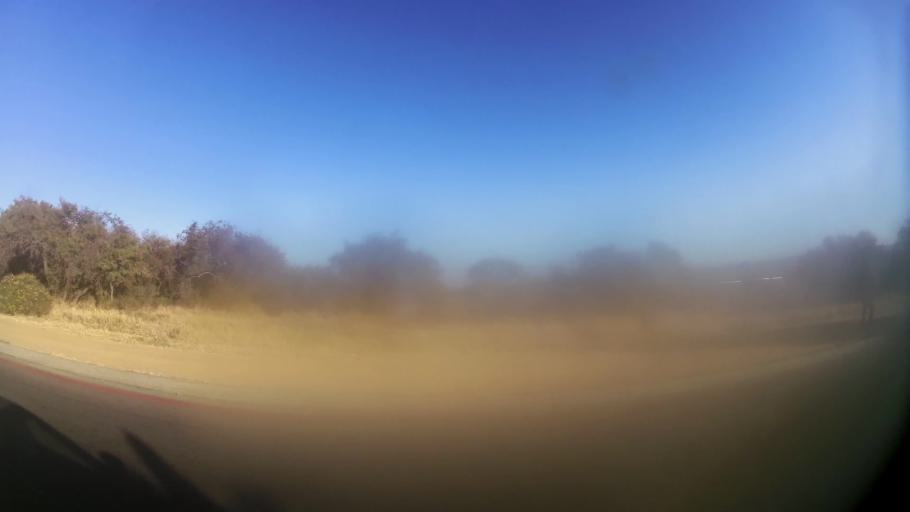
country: ZA
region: Gauteng
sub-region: City of Johannesburg Metropolitan Municipality
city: Midrand
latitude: -26.0076
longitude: 28.1220
